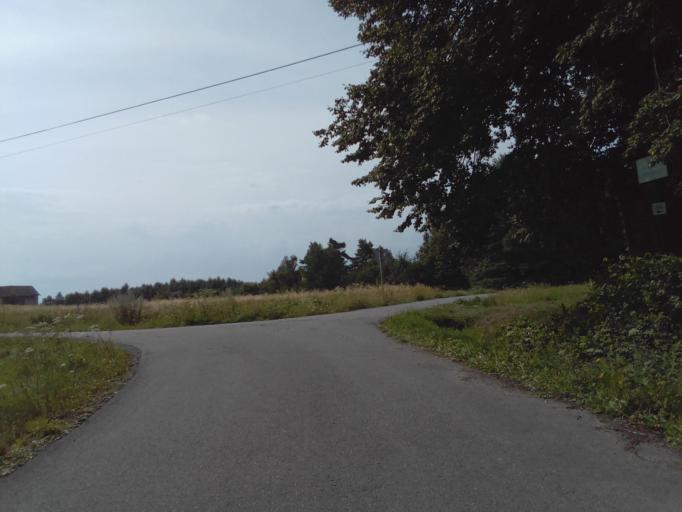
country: PL
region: Subcarpathian Voivodeship
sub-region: Powiat strzyzowski
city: Frysztak
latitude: 49.8683
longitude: 21.5258
